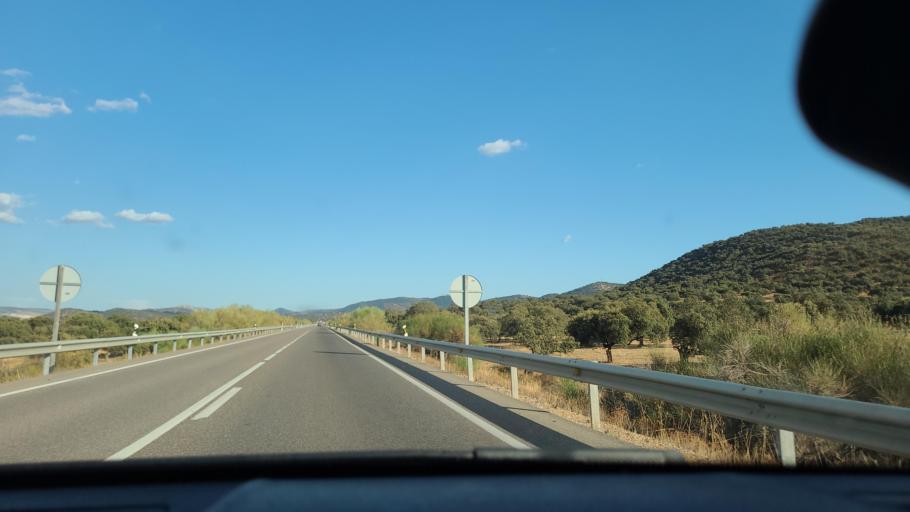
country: ES
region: Andalusia
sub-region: Province of Cordoba
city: Belmez
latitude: 38.2247
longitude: -5.1588
